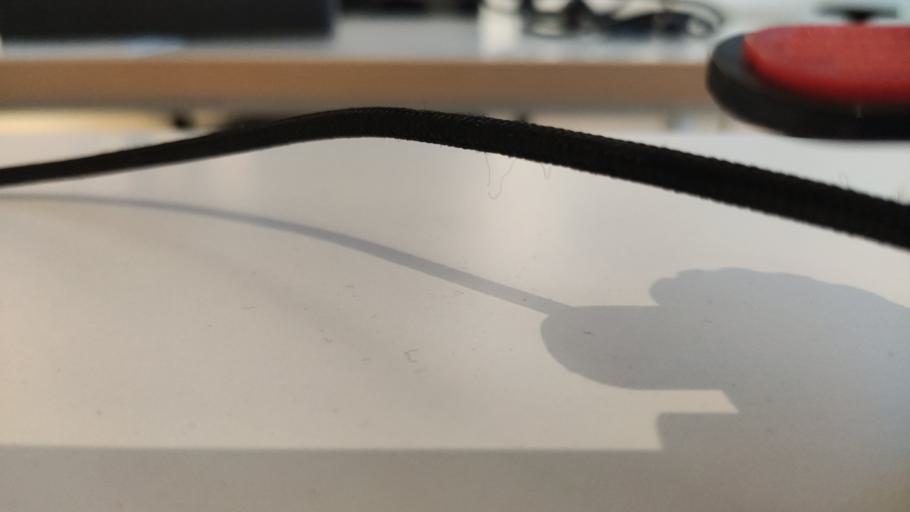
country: RU
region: Moskovskaya
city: Sychevo
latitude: 55.8359
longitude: 36.3286
